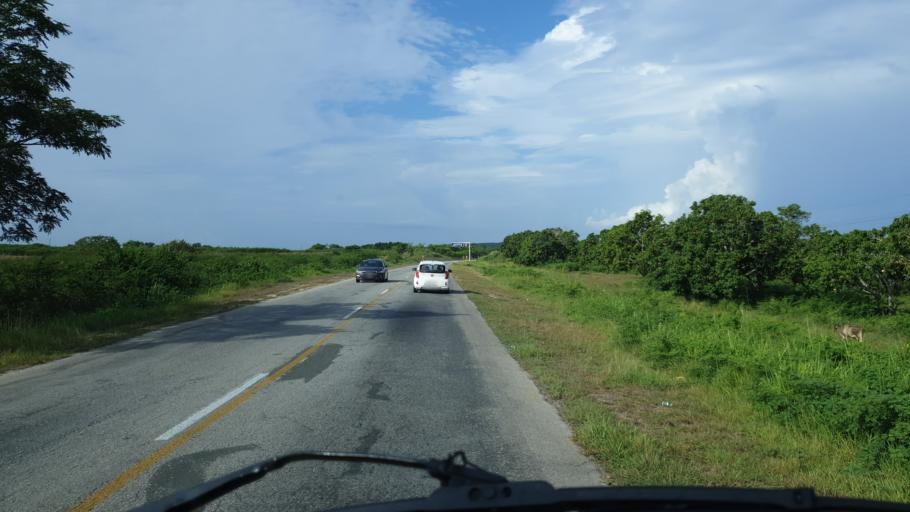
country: CU
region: Cienfuegos
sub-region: Municipio de Cienfuegos
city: Cienfuegos
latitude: 22.0796
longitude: -80.3891
